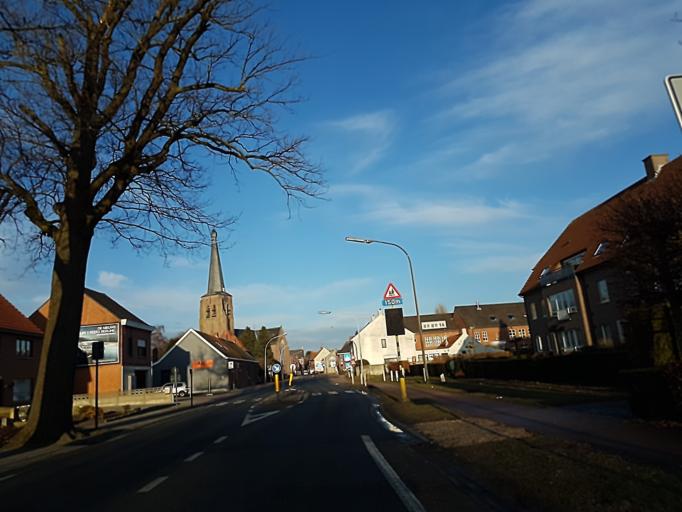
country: NL
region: North Brabant
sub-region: Gemeente Goirle
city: Goirle
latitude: 51.4446
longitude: 5.0374
